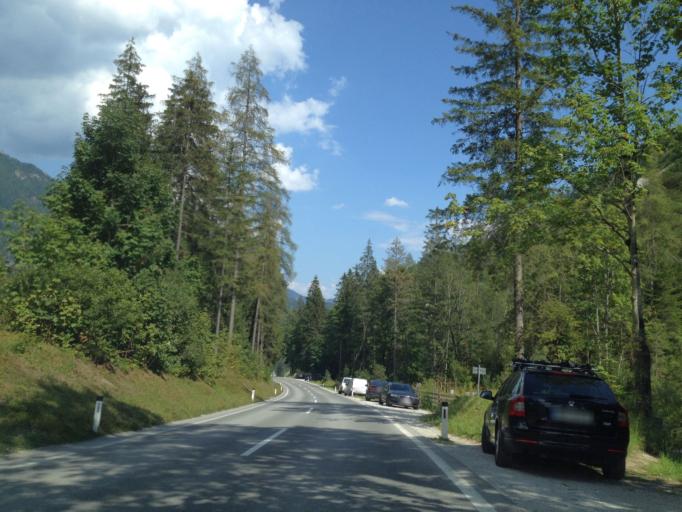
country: AT
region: Styria
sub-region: Politischer Bezirk Liezen
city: Schladming
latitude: 47.4241
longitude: 13.7002
